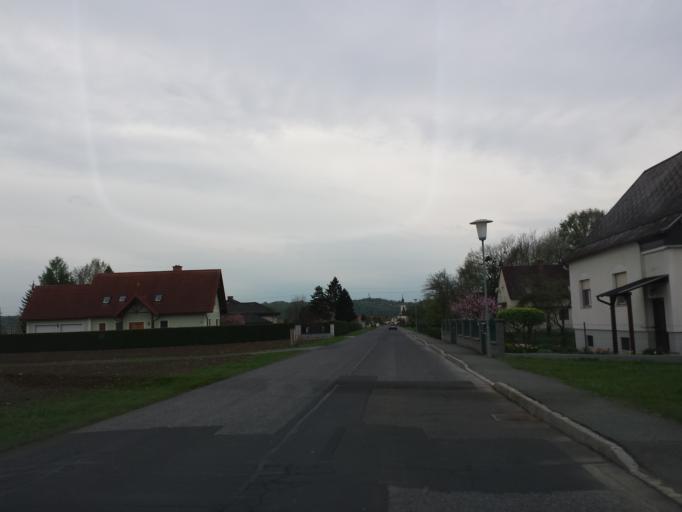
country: AT
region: Burgenland
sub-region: Politischer Bezirk Jennersdorf
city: Konigsdorf
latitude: 47.0105
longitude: 16.1754
